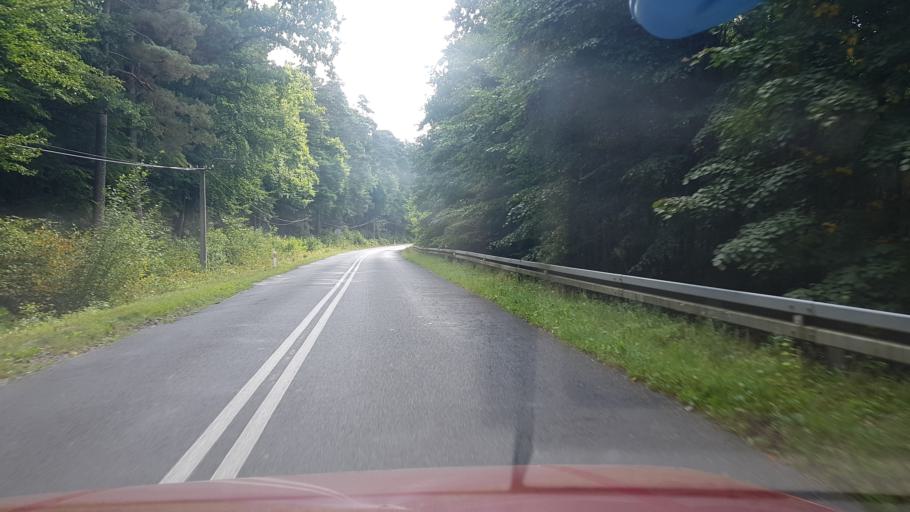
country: PL
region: West Pomeranian Voivodeship
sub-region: Powiat koszalinski
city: Polanow
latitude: 54.1167
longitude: 16.7053
